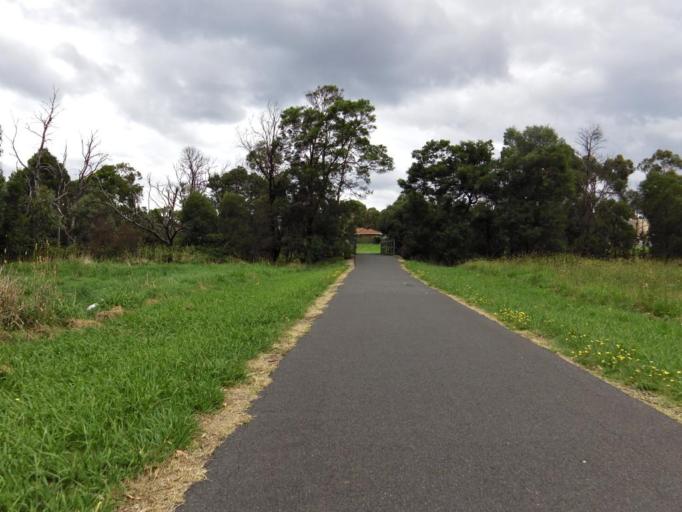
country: AU
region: Victoria
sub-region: Knox
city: Knoxfield
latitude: -37.9047
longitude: 145.2490
